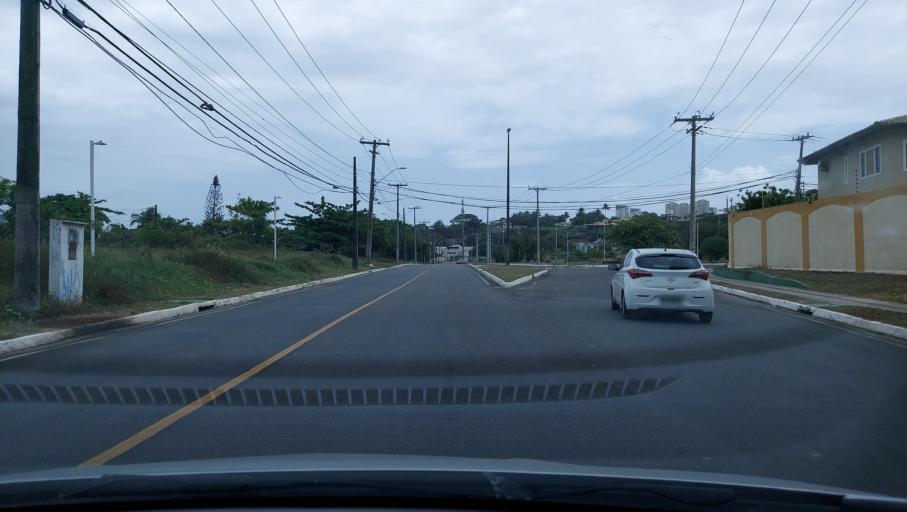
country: BR
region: Bahia
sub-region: Lauro De Freitas
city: Lauro de Freitas
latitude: -12.9512
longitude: -38.3916
